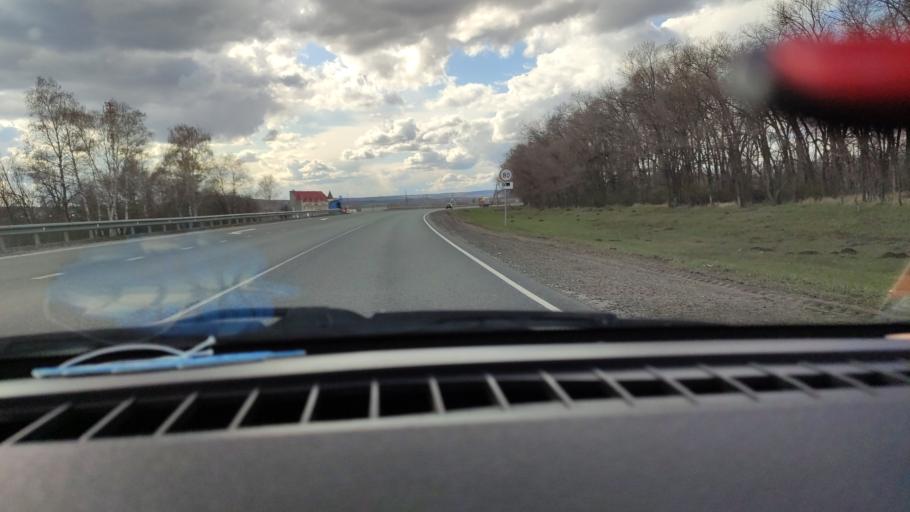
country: RU
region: Saratov
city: Tersa
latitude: 52.0850
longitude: 47.5530
